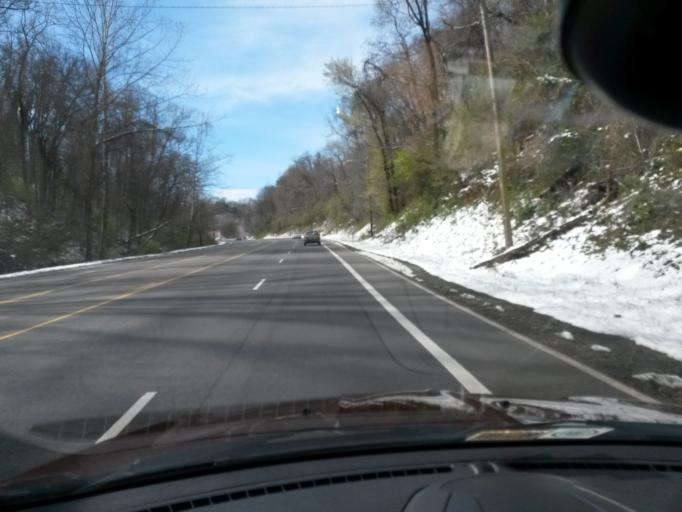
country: US
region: Virginia
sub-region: City of Roanoke
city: Cedar Bluff
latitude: 37.2427
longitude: -79.9646
